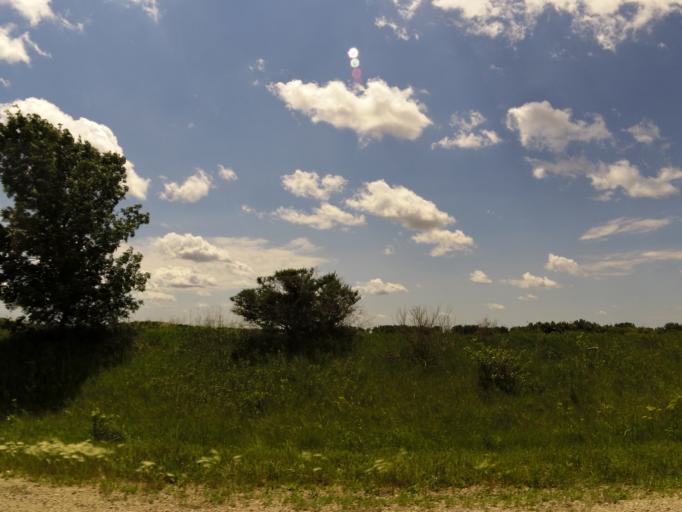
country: US
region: Iowa
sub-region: Fayette County
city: Oelwein
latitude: 42.7146
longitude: -91.9218
